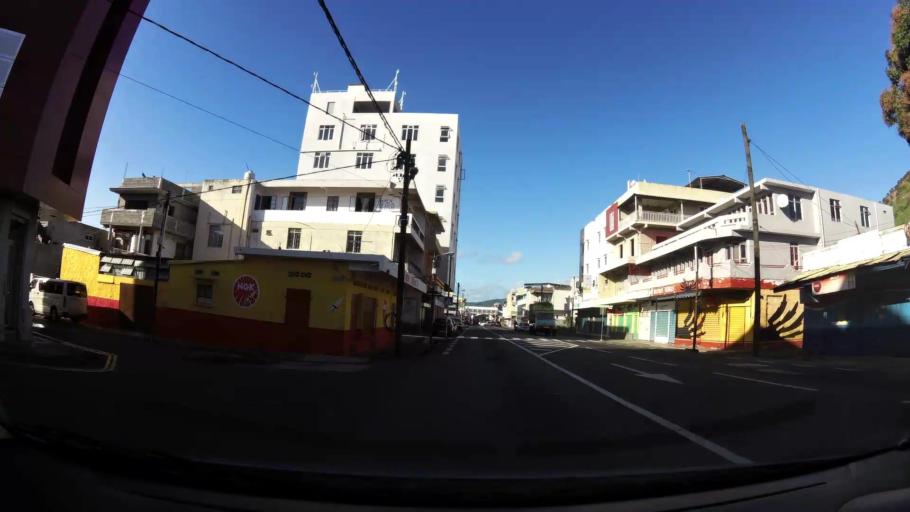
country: MU
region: Port Louis
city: Port Louis
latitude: -20.1672
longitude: 57.4872
